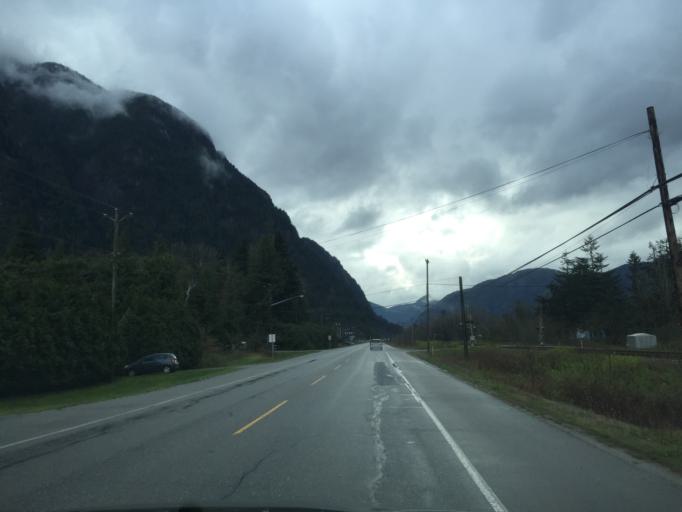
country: CA
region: British Columbia
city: Hope
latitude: 49.3665
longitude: -121.5092
